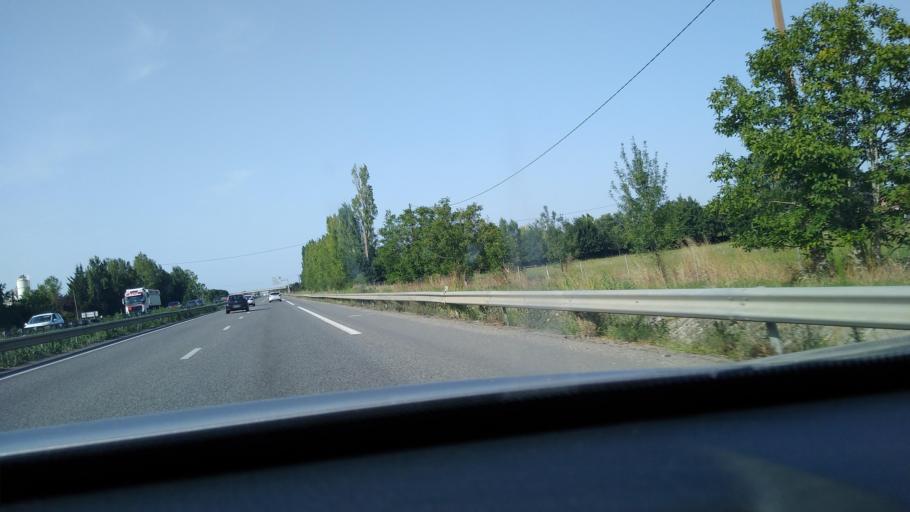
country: FR
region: Midi-Pyrenees
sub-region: Departement de la Haute-Garonne
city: Noe
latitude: 43.3774
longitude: 1.2793
